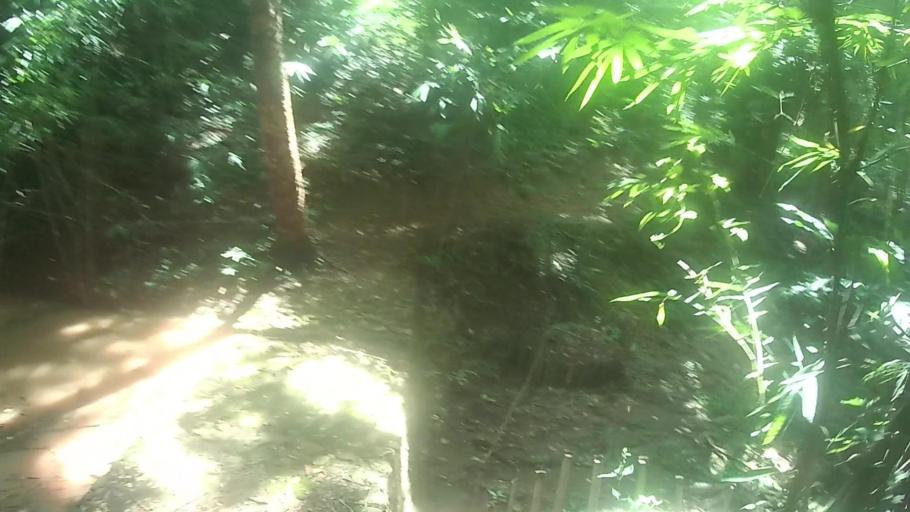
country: TH
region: Chiang Mai
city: Mae On
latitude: 18.8520
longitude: 99.2067
